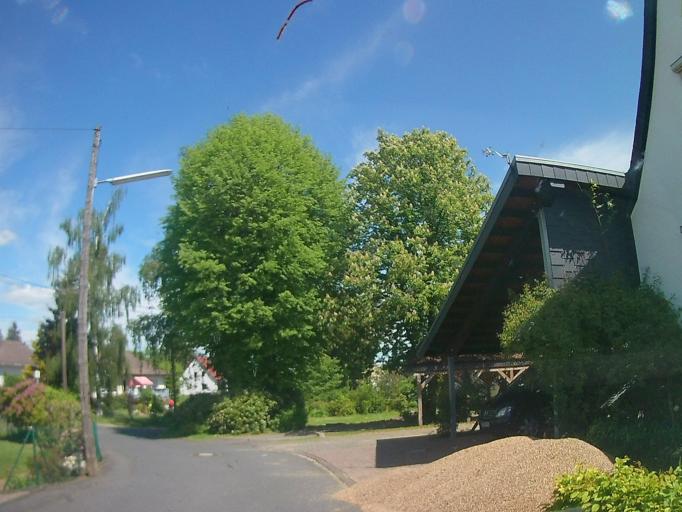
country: DE
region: Rheinland-Pfalz
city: Dierdorf
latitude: 50.5465
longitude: 7.6485
